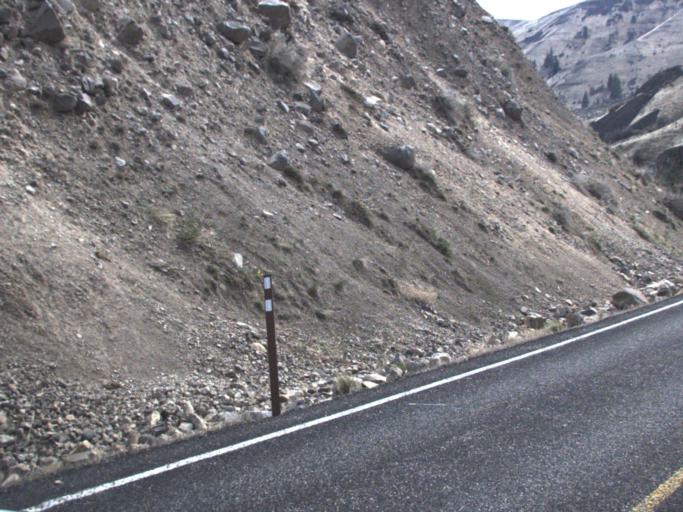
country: US
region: Washington
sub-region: Yakima County
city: Tieton
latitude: 46.7606
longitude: -120.8298
